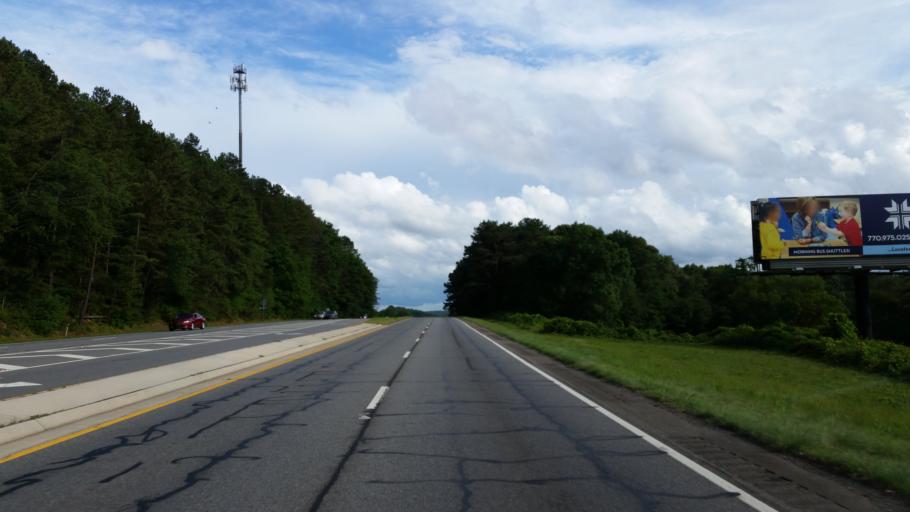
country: US
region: Georgia
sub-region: Bartow County
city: Emerson
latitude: 34.1261
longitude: -84.7513
